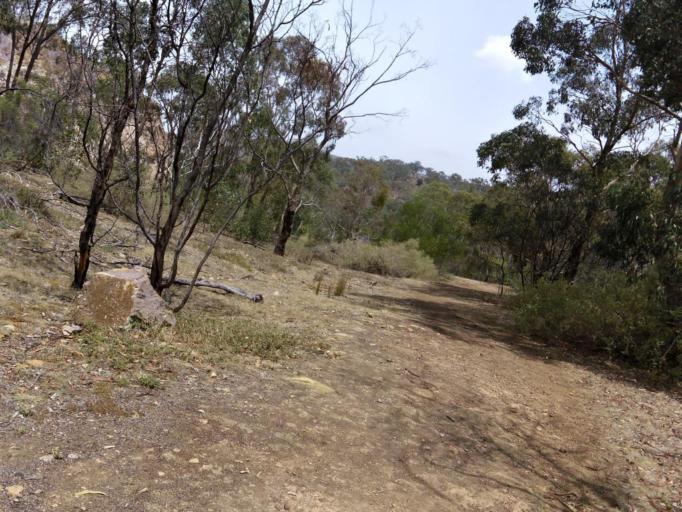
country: AU
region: Victoria
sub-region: Moorabool
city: Bacchus Marsh
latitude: -37.6630
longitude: 144.3642
